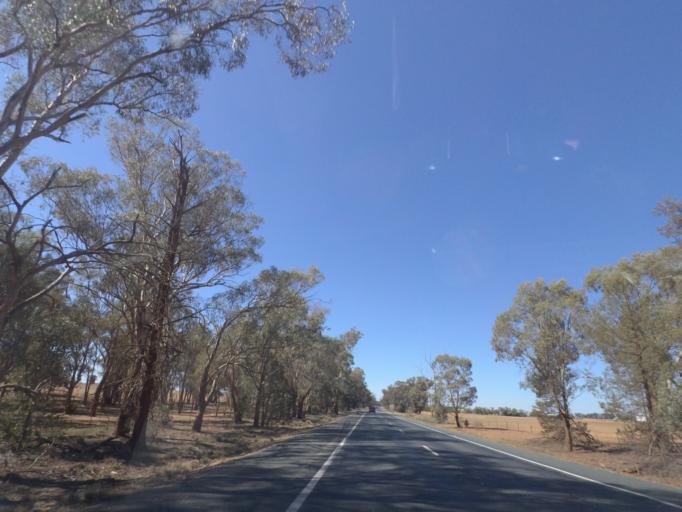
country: AU
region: New South Wales
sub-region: Bland
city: West Wyalong
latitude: -34.2028
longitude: 147.1101
